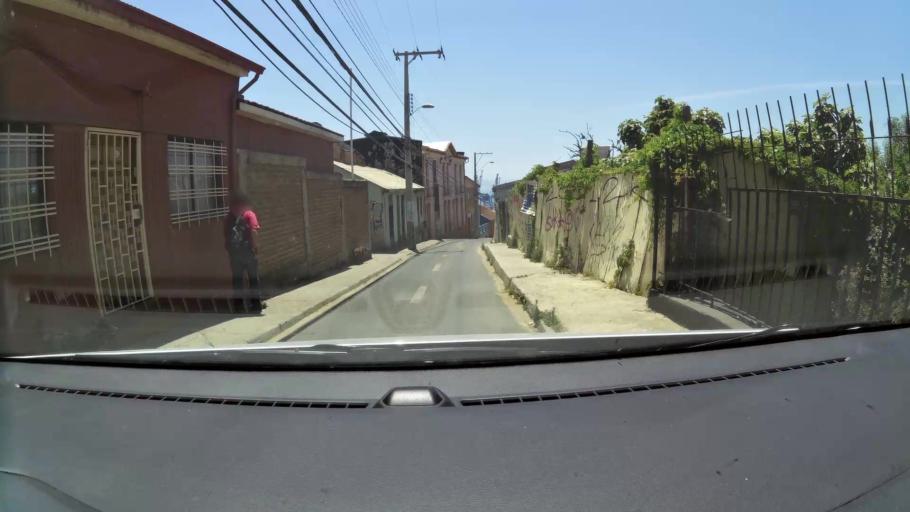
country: CL
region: Valparaiso
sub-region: Provincia de Valparaiso
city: Valparaiso
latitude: -33.0410
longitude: -71.6334
